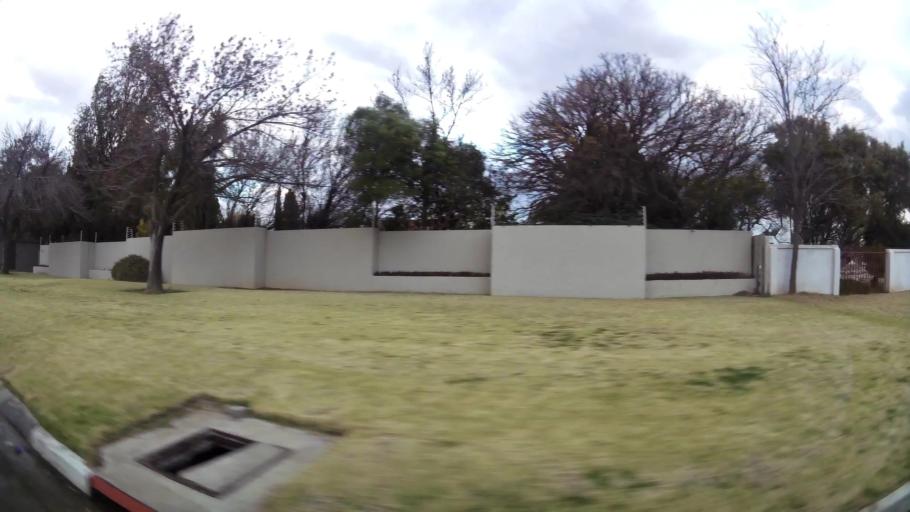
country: ZA
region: Orange Free State
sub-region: Lejweleputswa District Municipality
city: Welkom
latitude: -27.9555
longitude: 26.7361
